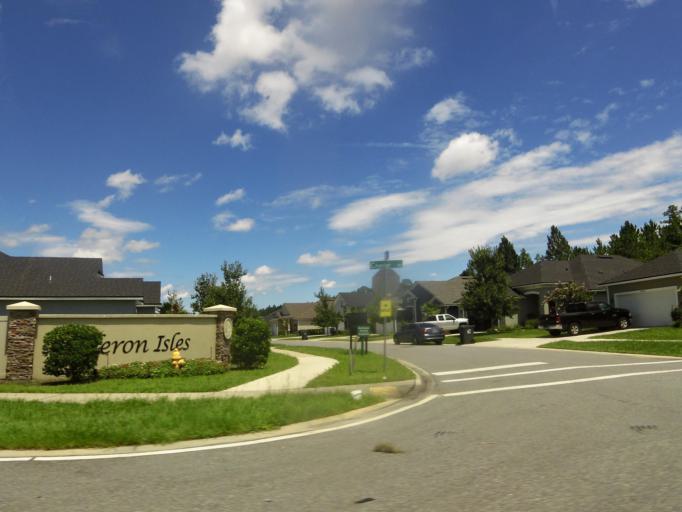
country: US
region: Florida
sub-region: Nassau County
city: Yulee
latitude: 30.6480
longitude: -81.5439
